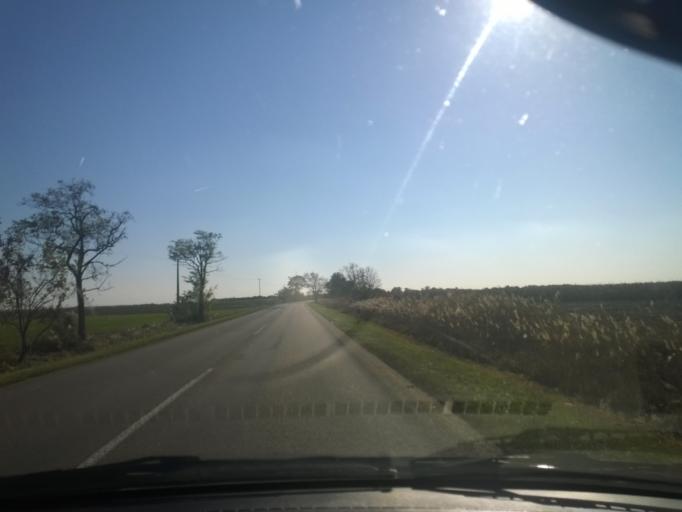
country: HU
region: Csongrad
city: Szegvar
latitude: 46.5667
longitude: 20.3114
